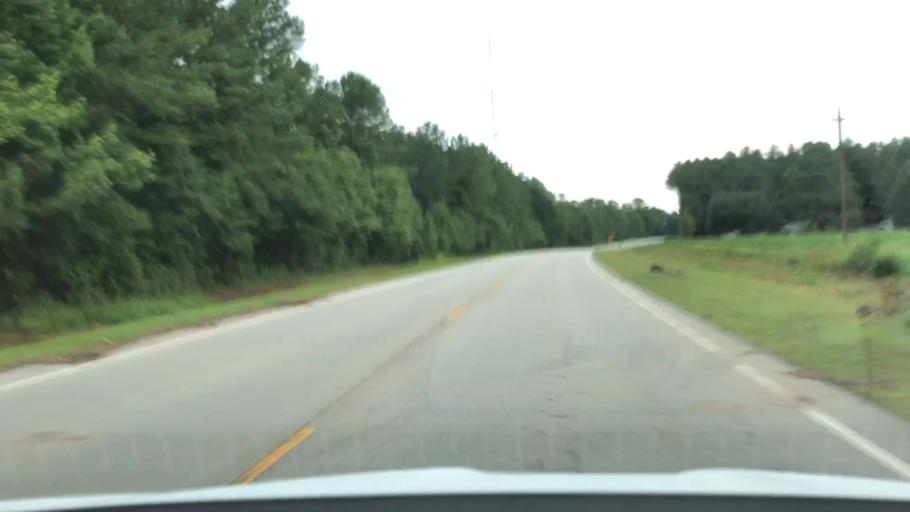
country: US
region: North Carolina
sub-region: Jones County
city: Trenton
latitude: 35.0378
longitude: -77.3459
